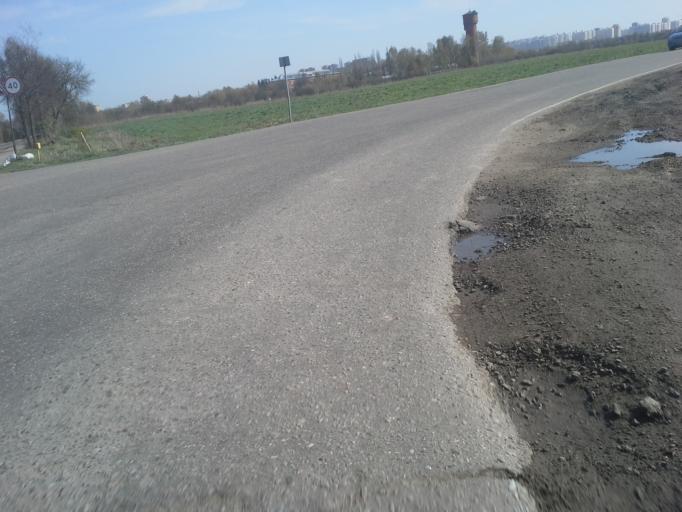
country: RU
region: Moskovskaya
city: Dubrovitsy
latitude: 55.4477
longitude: 37.4781
